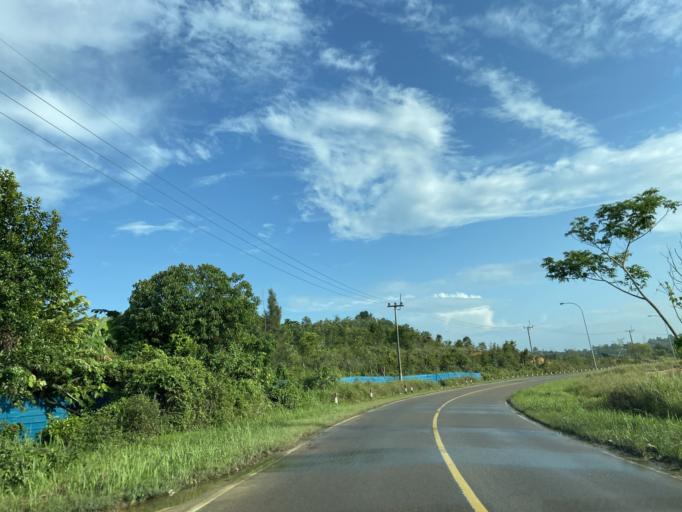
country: SG
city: Singapore
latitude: 0.9511
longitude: 104.0528
